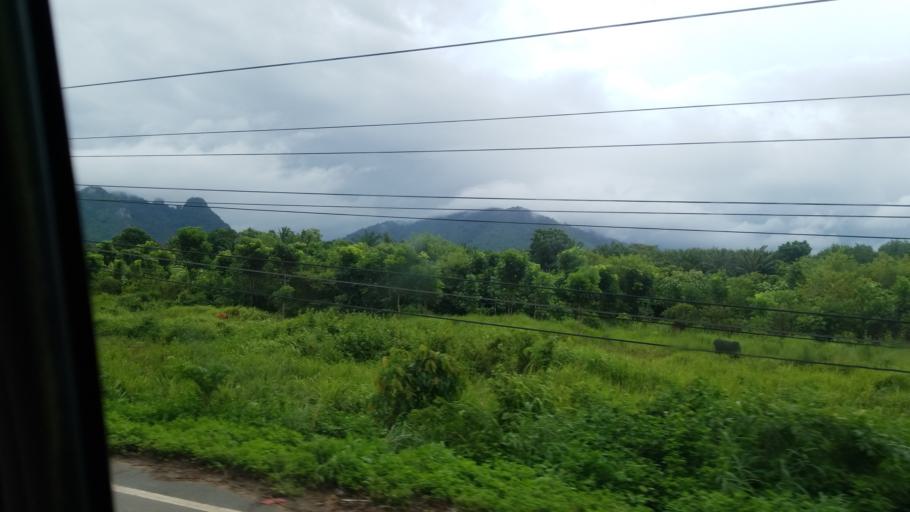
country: TH
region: Krabi
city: Nuea Khlong
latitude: 8.1821
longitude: 98.9599
